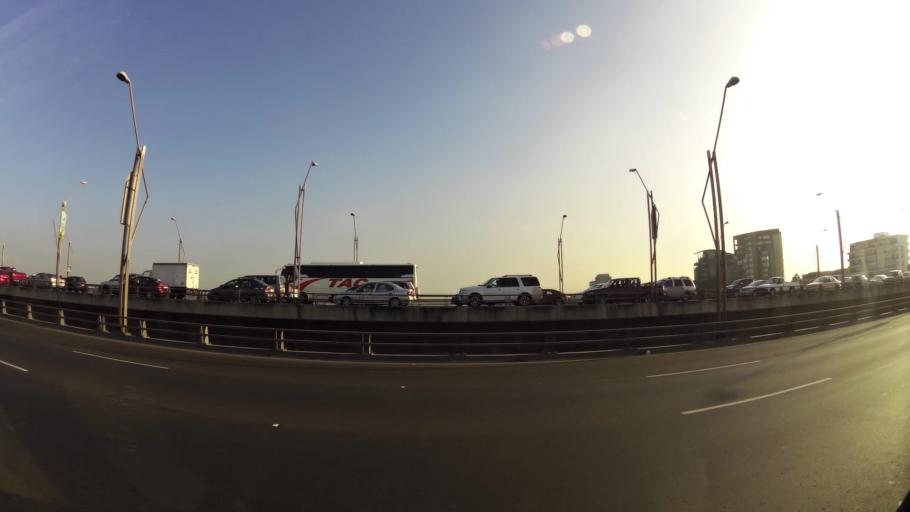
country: EC
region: Guayas
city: Eloy Alfaro
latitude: -2.1532
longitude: -79.8710
